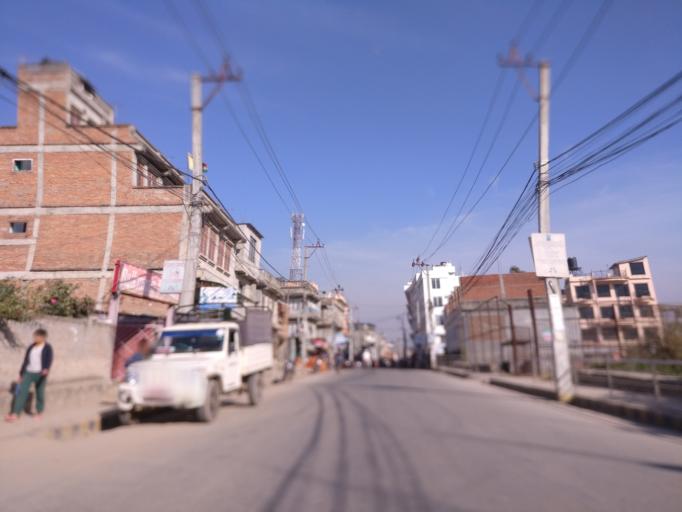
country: NP
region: Central Region
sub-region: Bagmati Zone
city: Patan
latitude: 27.6716
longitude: 85.3377
